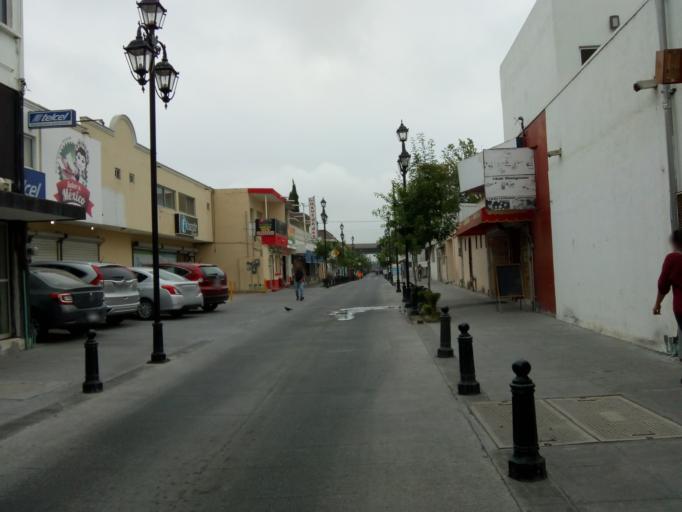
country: MX
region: Nuevo Leon
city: Guadalupe
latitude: 25.6777
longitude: -100.2597
